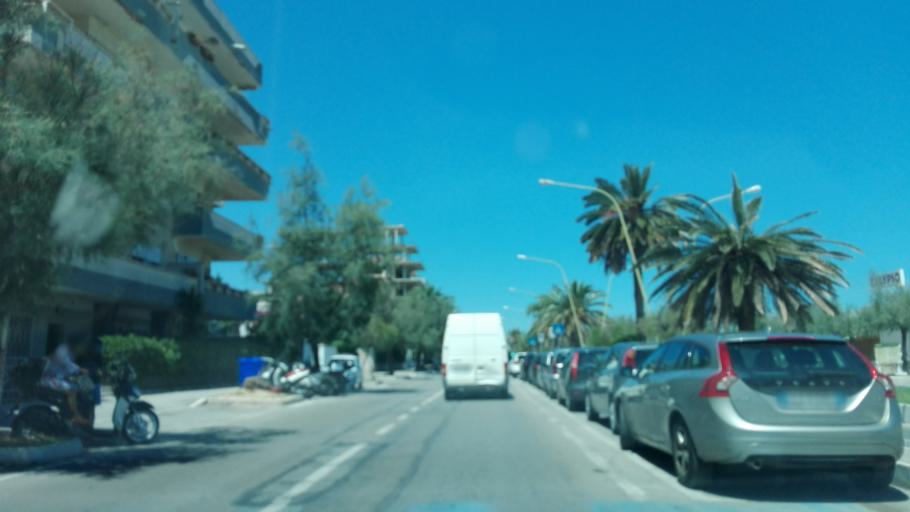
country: IT
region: Abruzzo
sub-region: Provincia di Pescara
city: Pescara
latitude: 42.4808
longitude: 14.2005
